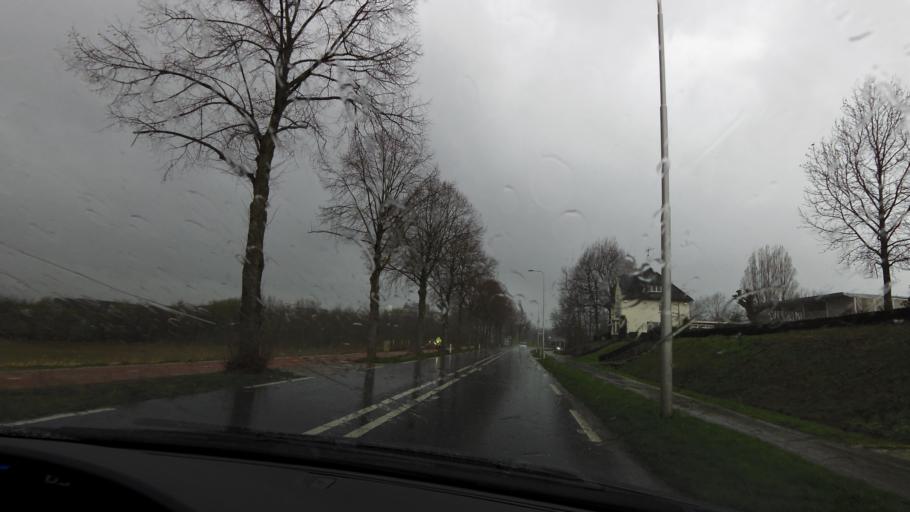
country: NL
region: Limburg
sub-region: Gemeente Beek
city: Beek
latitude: 50.9339
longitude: 5.7846
